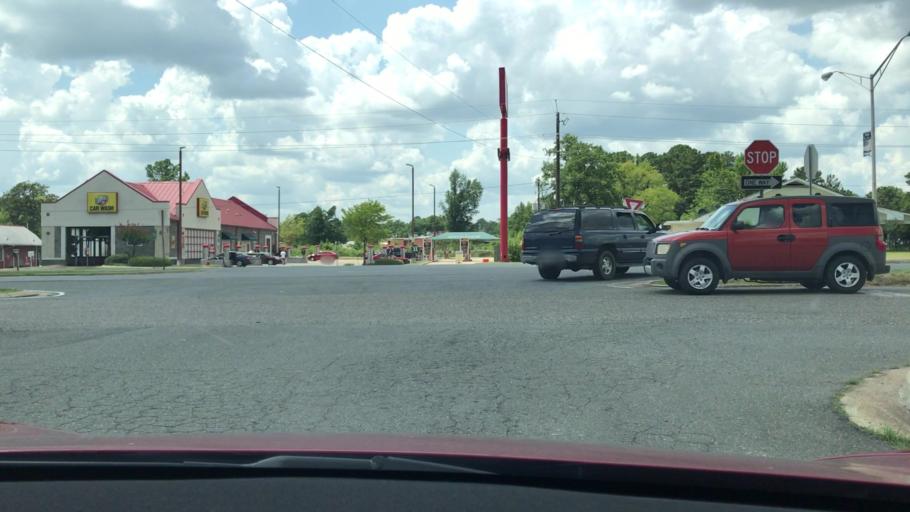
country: US
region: Louisiana
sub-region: De Soto Parish
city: Stonewall
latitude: 32.3993
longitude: -93.8065
